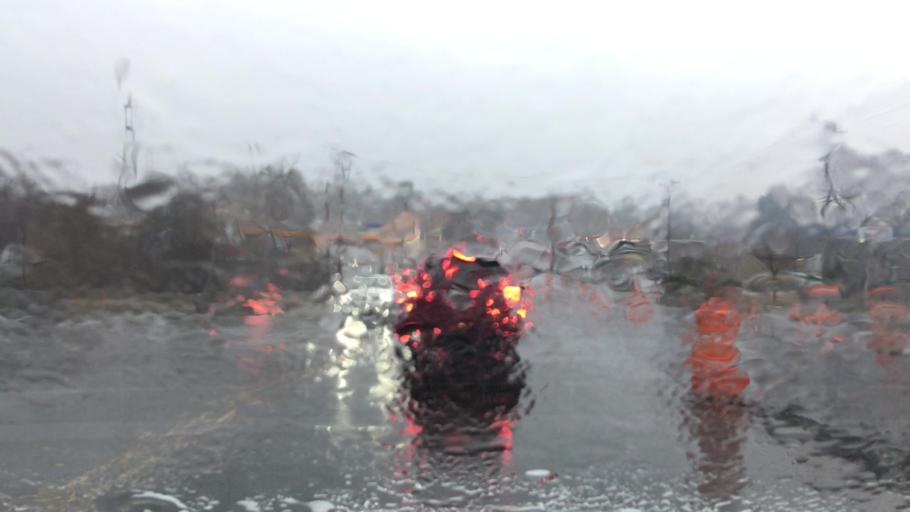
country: US
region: New Hampshire
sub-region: Rockingham County
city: Derry
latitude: 42.8721
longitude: -71.3381
